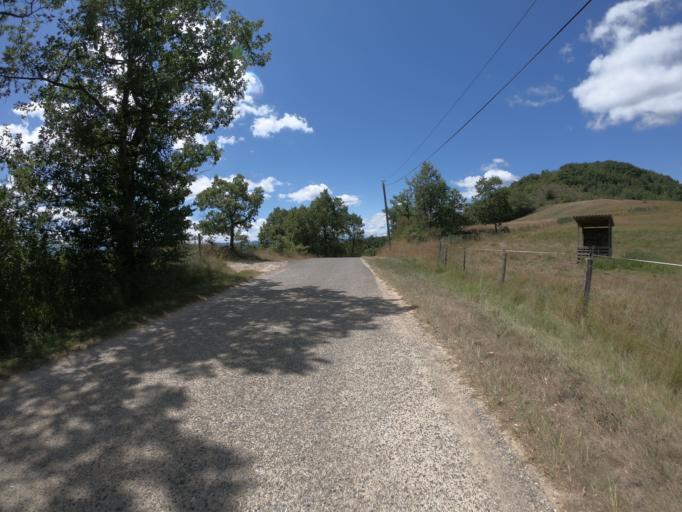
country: FR
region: Midi-Pyrenees
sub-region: Departement de l'Ariege
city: Mirepoix
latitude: 43.0492
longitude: 1.8349
